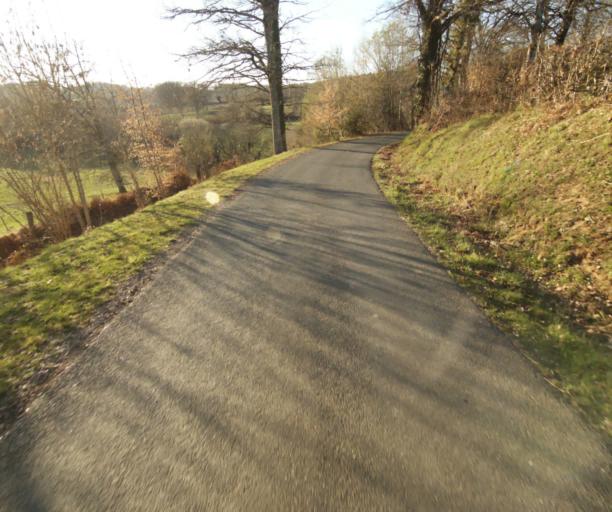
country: FR
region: Limousin
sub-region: Departement de la Correze
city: Saint-Clement
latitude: 45.3609
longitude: 1.6858
